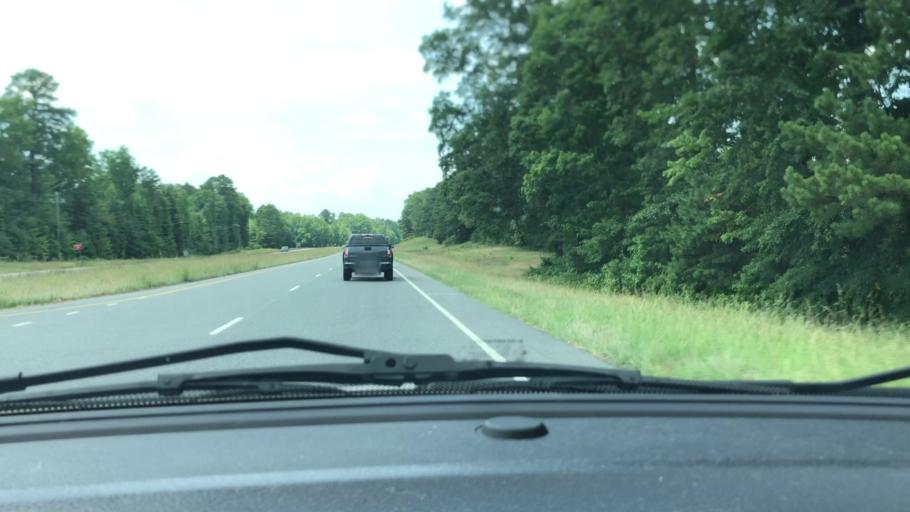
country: US
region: North Carolina
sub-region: Chatham County
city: Farmville
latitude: 35.5256
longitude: -79.2278
